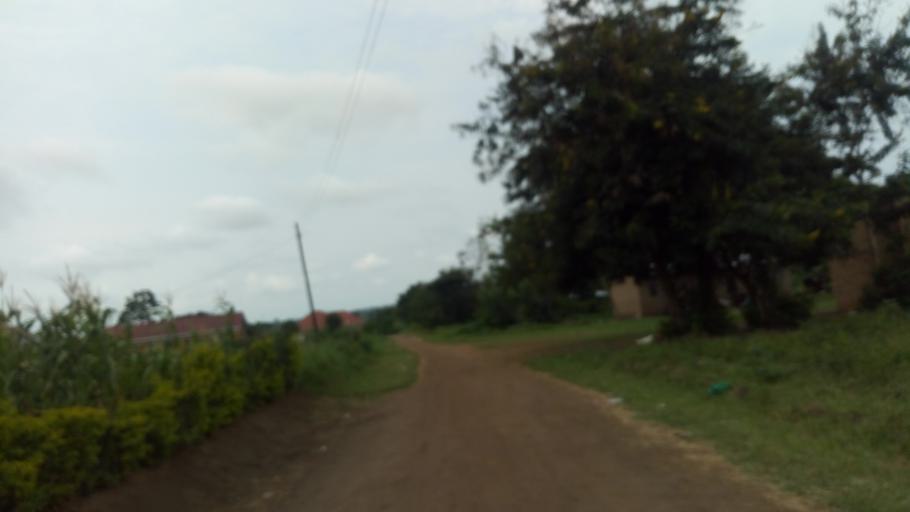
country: UG
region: Western Region
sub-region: Kiryandongo District
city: Kiryandongo
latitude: 1.7974
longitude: 32.0084
